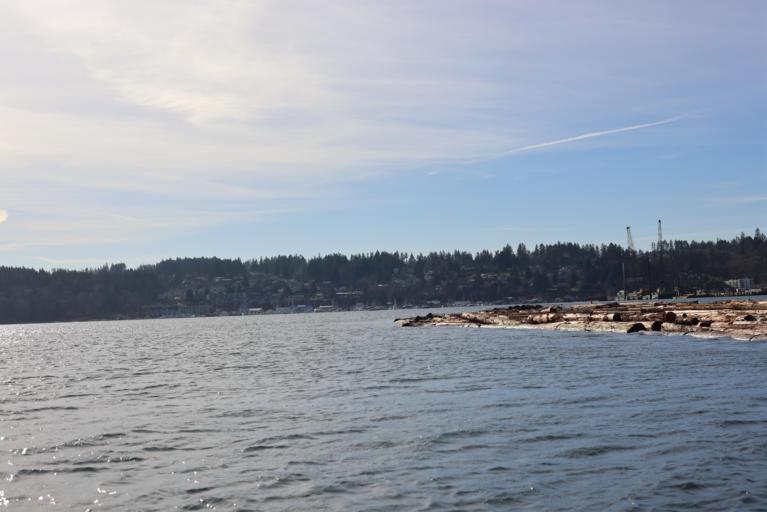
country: CA
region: British Columbia
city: Duncan
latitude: 48.7554
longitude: -123.6218
